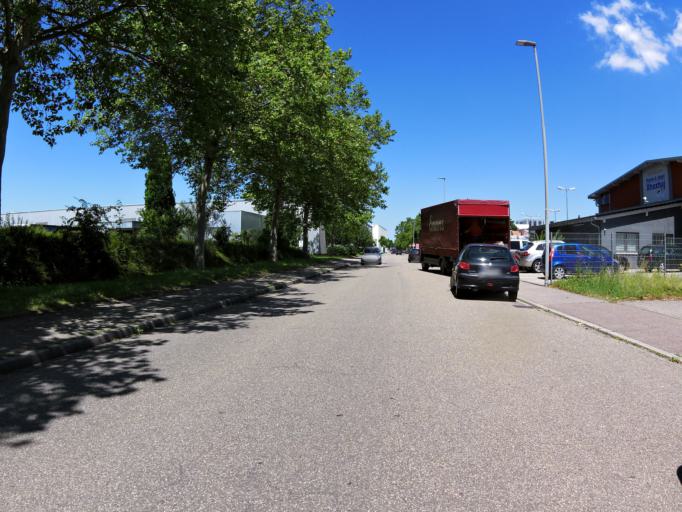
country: DE
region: Baden-Wuerttemberg
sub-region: Freiburg Region
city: Lahr
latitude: 48.3401
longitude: 7.8287
